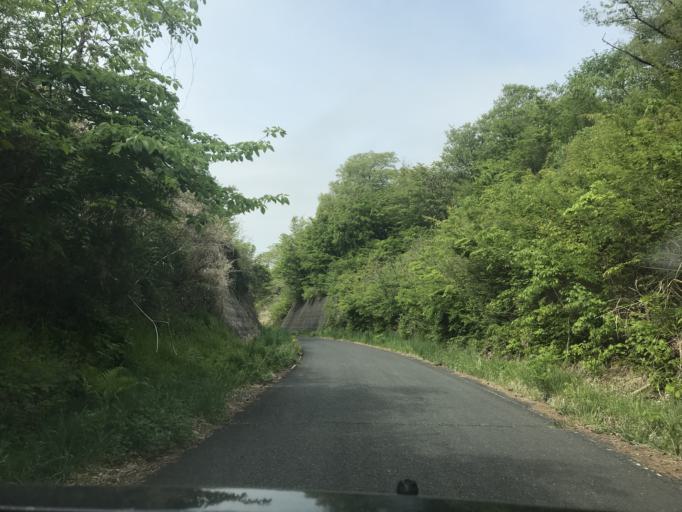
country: JP
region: Iwate
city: Ichinoseki
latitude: 38.8656
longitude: 141.0634
